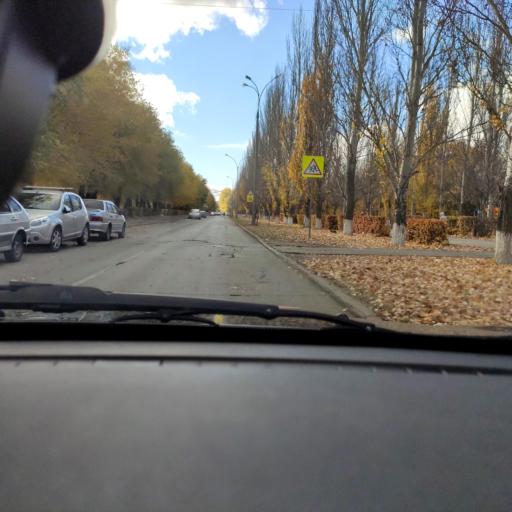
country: RU
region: Samara
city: Tol'yatti
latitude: 53.5319
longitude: 49.2925
